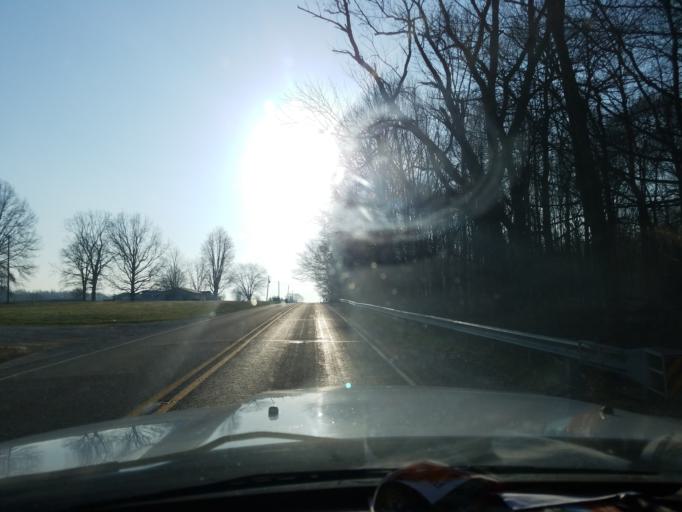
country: US
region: Indiana
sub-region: Clay County
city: Middlebury
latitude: 39.3880
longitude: -87.1650
